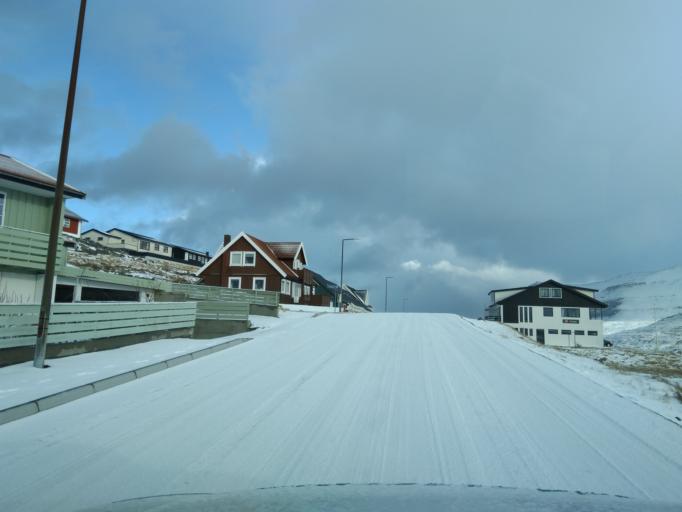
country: FO
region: Eysturoy
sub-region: Eidi
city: Eidi
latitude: 62.3006
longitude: -7.0977
